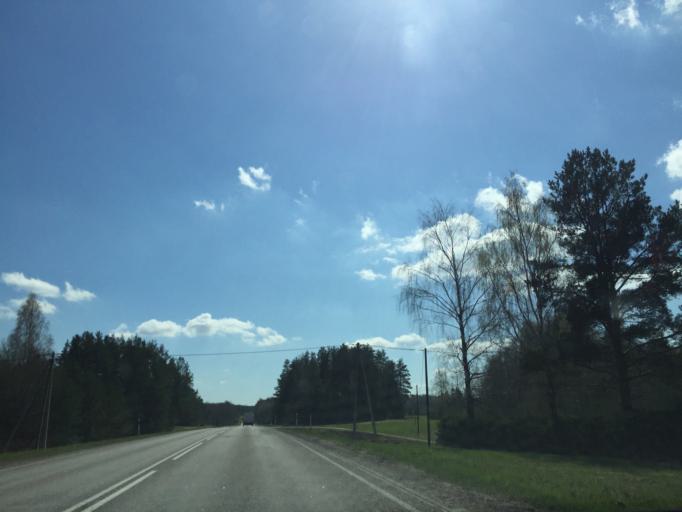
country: EE
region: Tartu
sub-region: Elva linn
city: Elva
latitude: 58.0768
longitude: 26.2065
